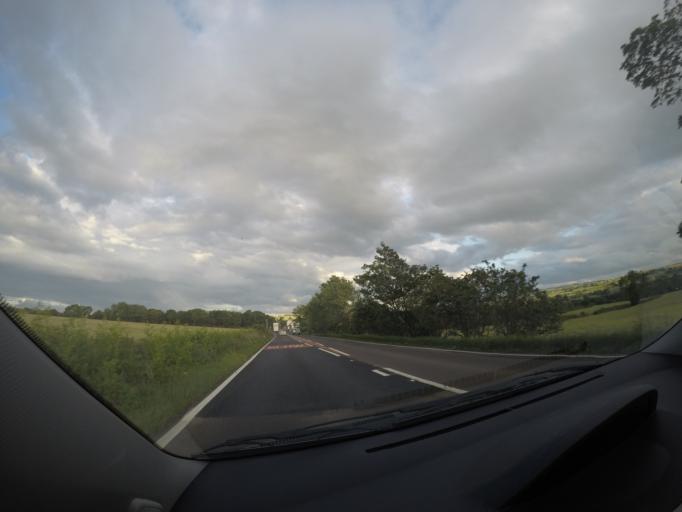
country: GB
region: England
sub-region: County Durham
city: Hutton Magna
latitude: 54.4787
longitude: -1.7769
